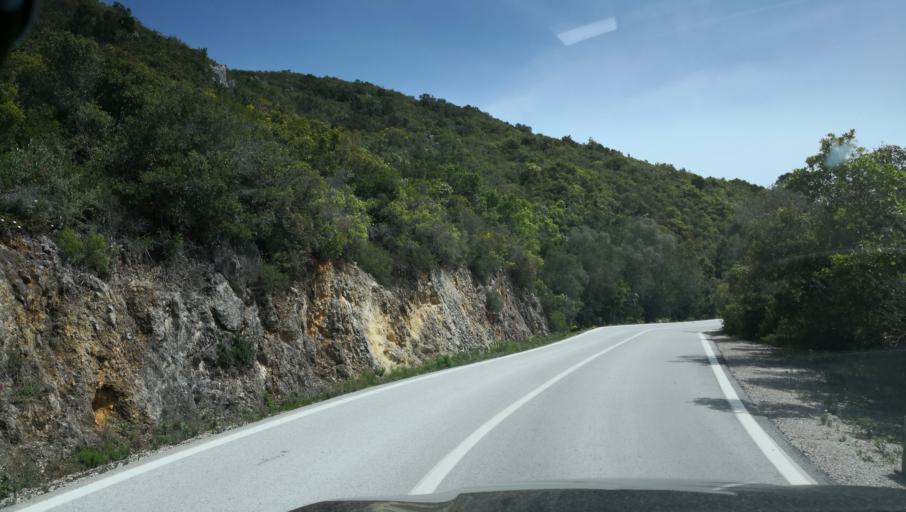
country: PT
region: Setubal
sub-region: Sesimbra
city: Sesimbra
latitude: 38.4624
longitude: -9.0098
